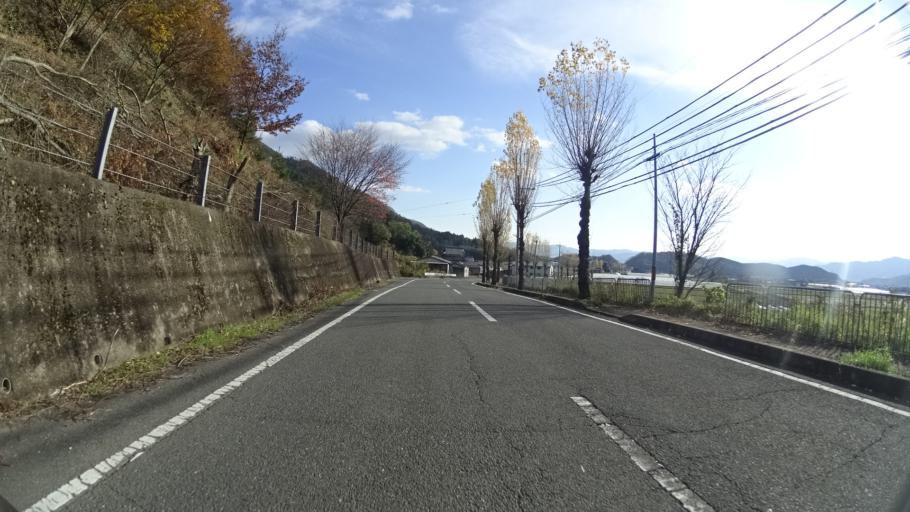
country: JP
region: Kyoto
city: Kameoka
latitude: 35.0827
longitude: 135.5653
